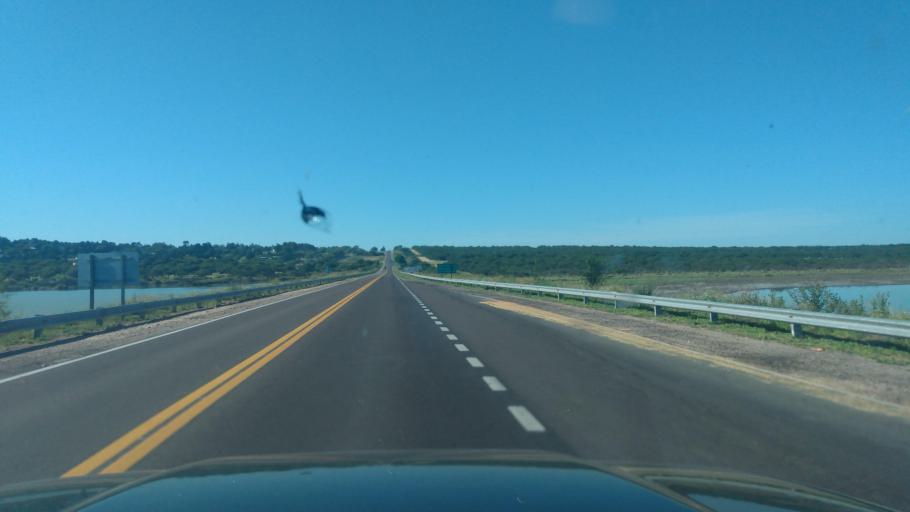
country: AR
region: La Pampa
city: Santa Rosa
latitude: -36.7164
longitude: -64.2831
